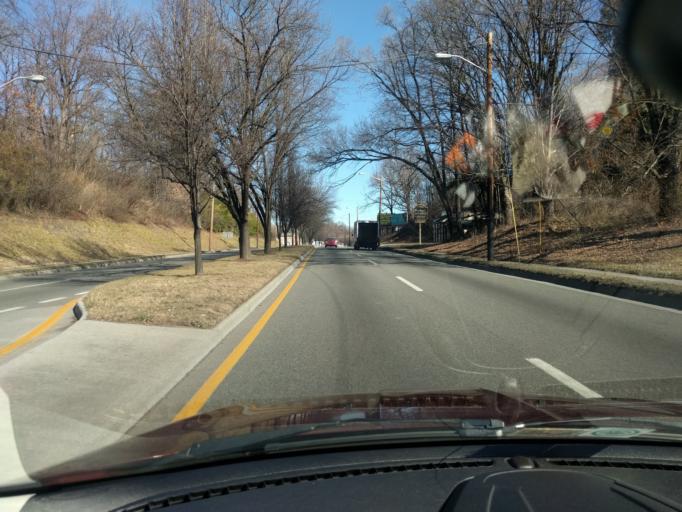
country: US
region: Virginia
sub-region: Roanoke County
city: Vinton
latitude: 37.2873
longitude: -79.9137
